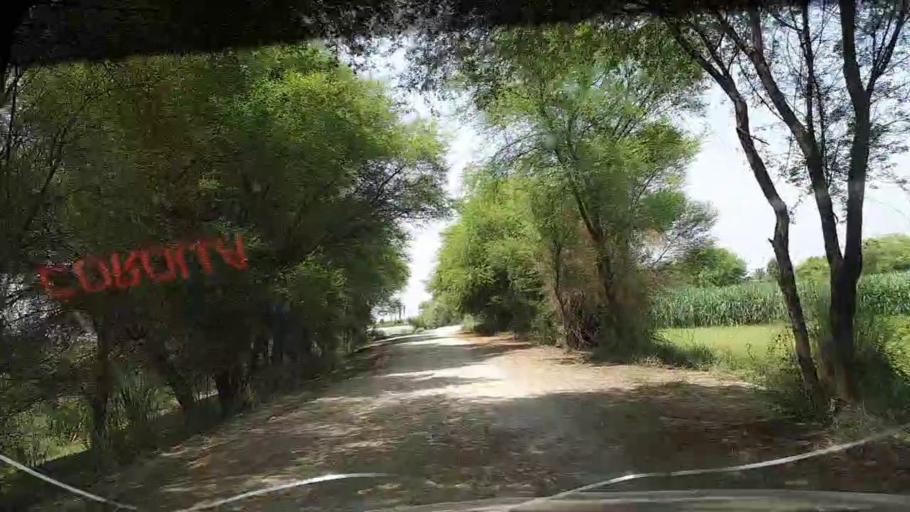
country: PK
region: Sindh
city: Ghotki
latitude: 28.0970
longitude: 69.3122
